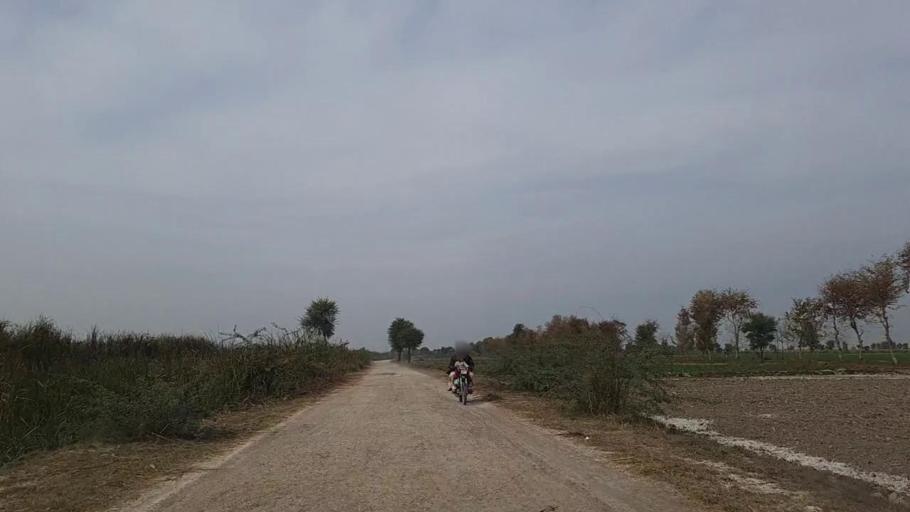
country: PK
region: Sindh
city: Daur
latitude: 26.4196
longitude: 68.4217
